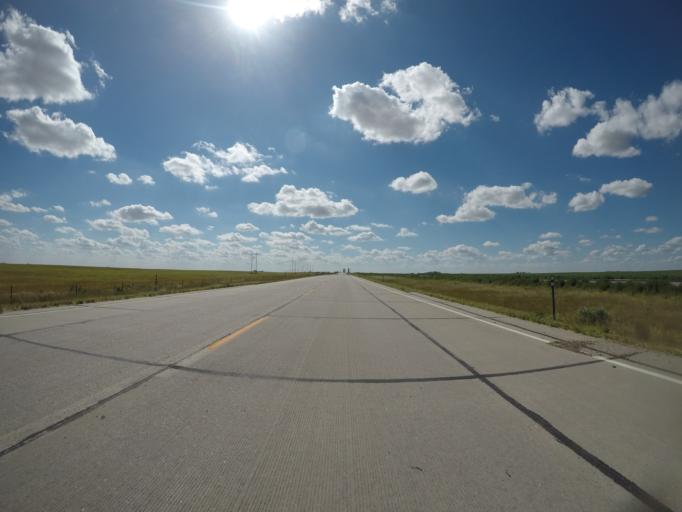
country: US
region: Colorado
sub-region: Phillips County
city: Holyoke
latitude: 40.6069
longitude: -102.4382
